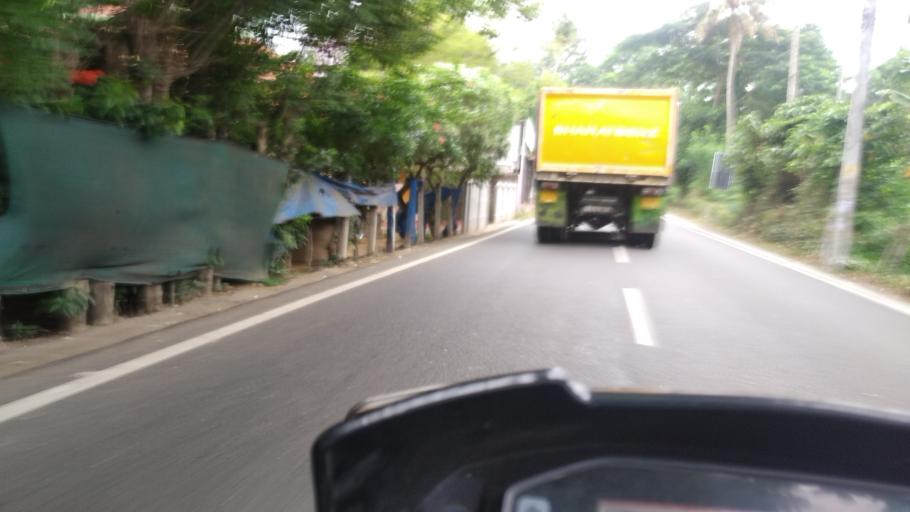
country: IN
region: Kerala
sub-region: Ernakulam
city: Aluva
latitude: 10.1549
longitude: 76.2780
